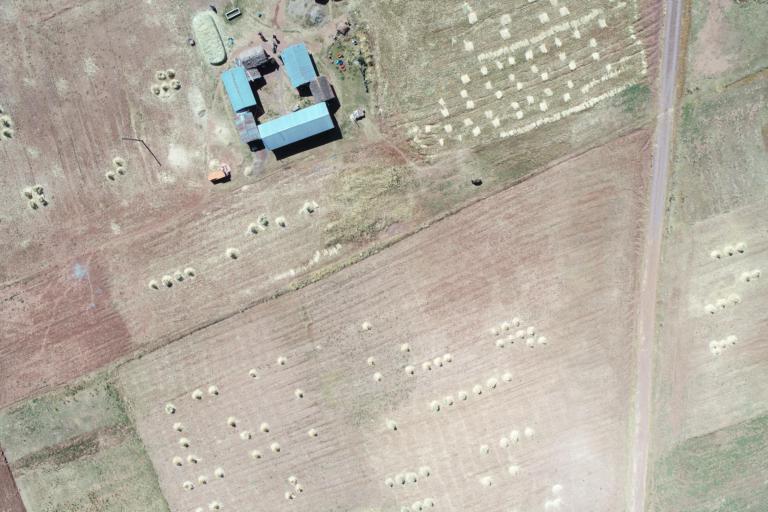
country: BO
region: La Paz
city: Tiahuanaco
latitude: -16.5906
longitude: -68.7717
